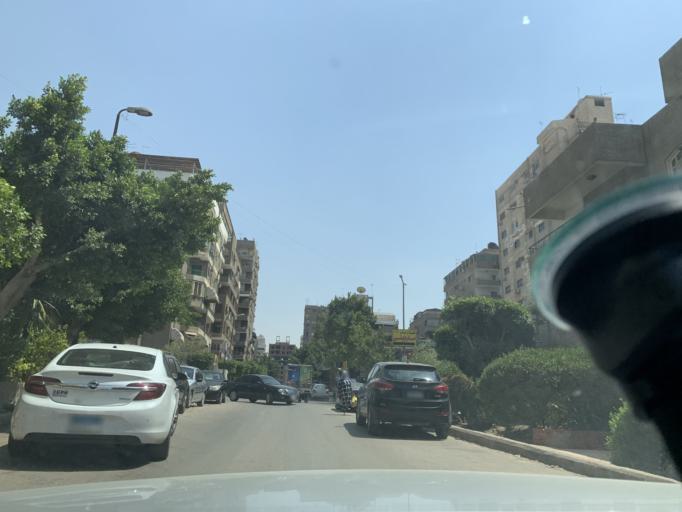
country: EG
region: Muhafazat al Qahirah
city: Cairo
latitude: 30.0603
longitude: 31.3498
